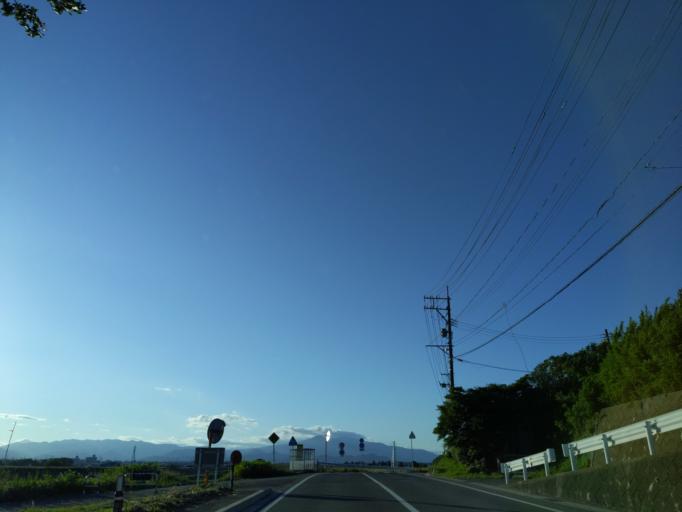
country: JP
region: Fukushima
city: Koriyama
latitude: 37.3954
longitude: 140.4119
